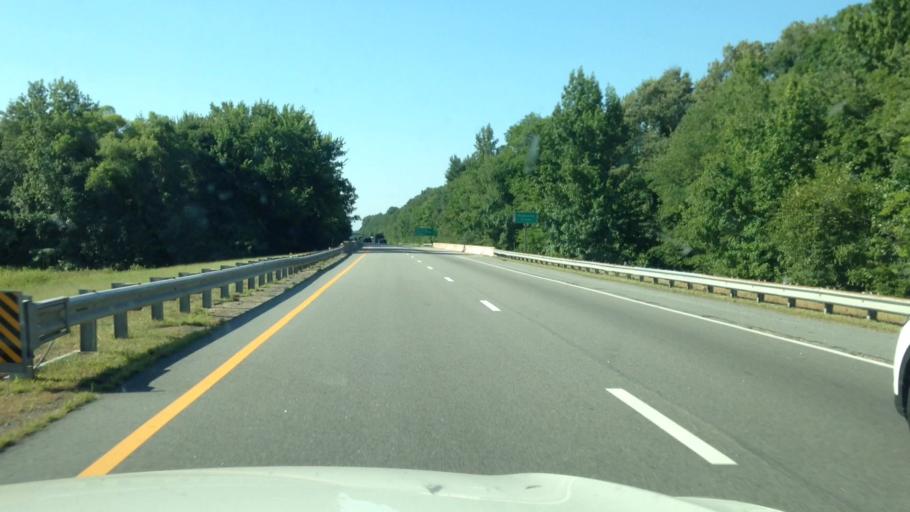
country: US
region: Virginia
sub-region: Sussex County
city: Sussex
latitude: 36.9912
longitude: -77.3919
